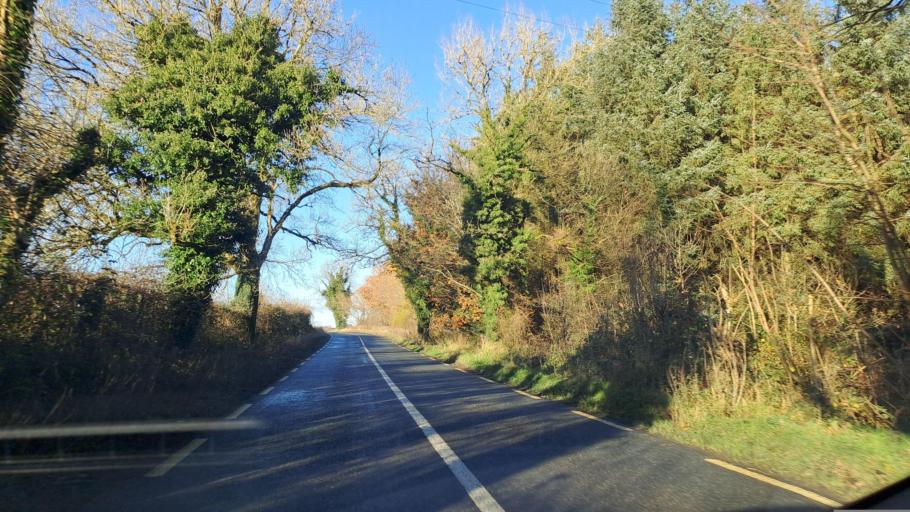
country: IE
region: Ulster
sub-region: An Cabhan
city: Mullagh
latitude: 53.8602
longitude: -6.9554
